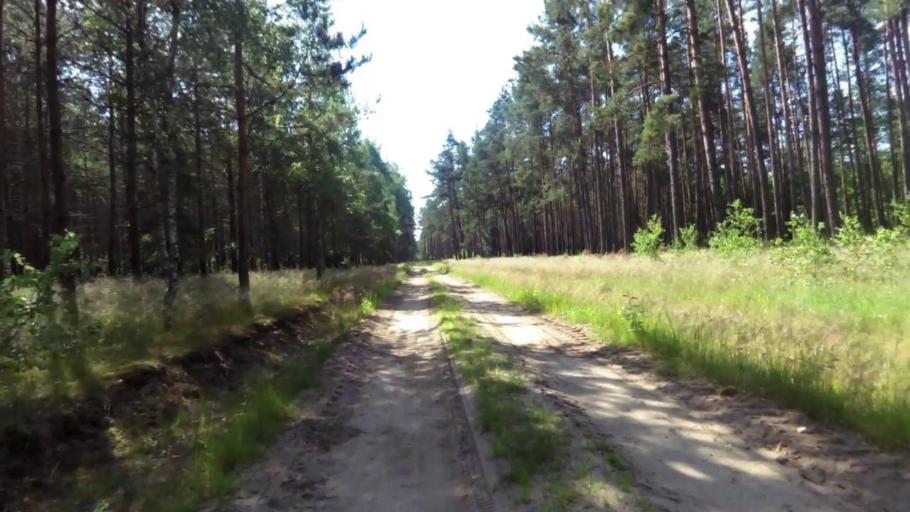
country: PL
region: West Pomeranian Voivodeship
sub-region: Powiat swidwinski
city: Polczyn-Zdroj
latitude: 53.8670
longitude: 16.1223
